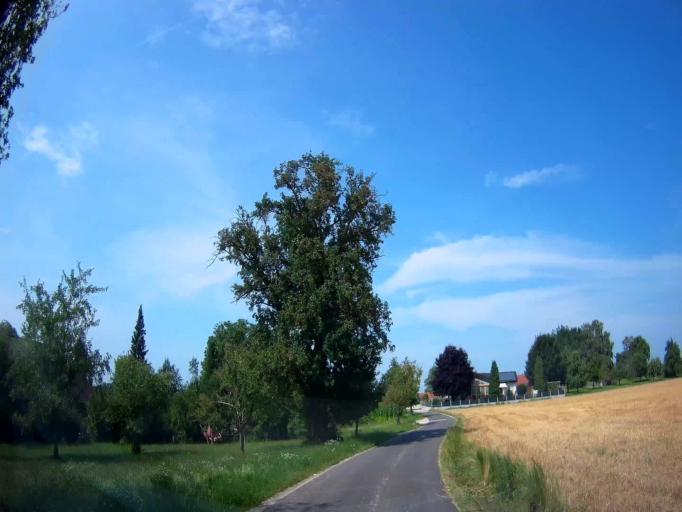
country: AT
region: Upper Austria
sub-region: Politischer Bezirk Kirchdorf an der Krems
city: Kremsmunster
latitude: 48.0772
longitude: 14.0985
